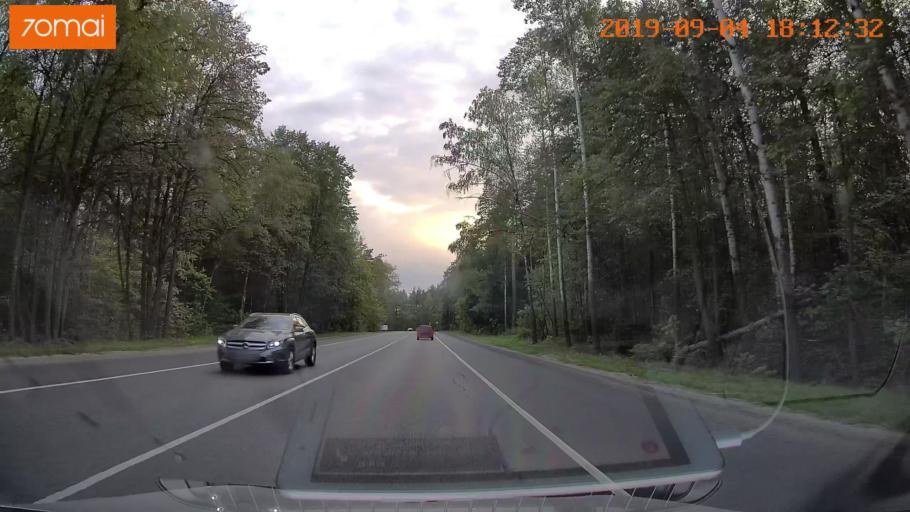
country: RU
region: Moskovskaya
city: Lopatinskiy
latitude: 55.3697
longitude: 38.7403
